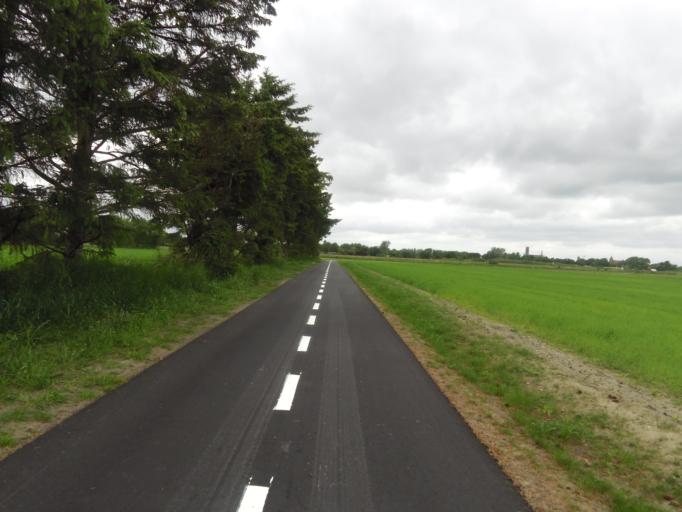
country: DK
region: South Denmark
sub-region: Esbjerg Kommune
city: Ribe
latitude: 55.3144
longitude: 8.7663
